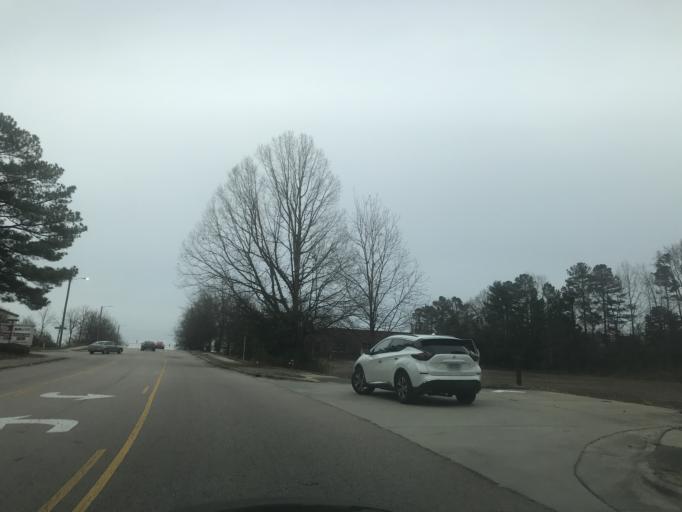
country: US
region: North Carolina
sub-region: Wake County
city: Raleigh
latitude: 35.8716
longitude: -78.5850
